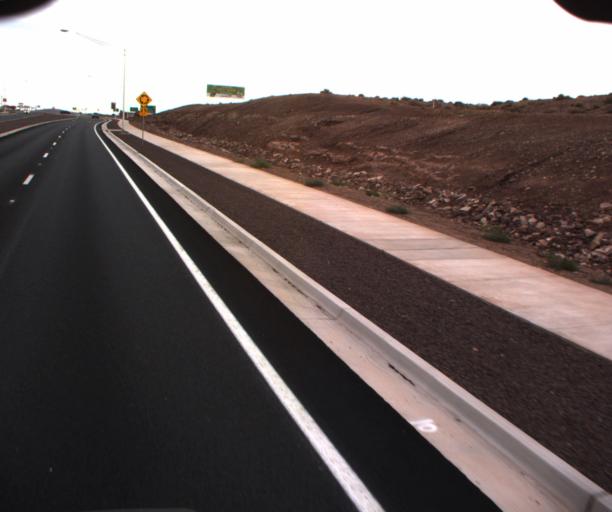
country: US
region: Arizona
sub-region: Coconino County
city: Tuba City
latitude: 35.8575
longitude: -111.4227
